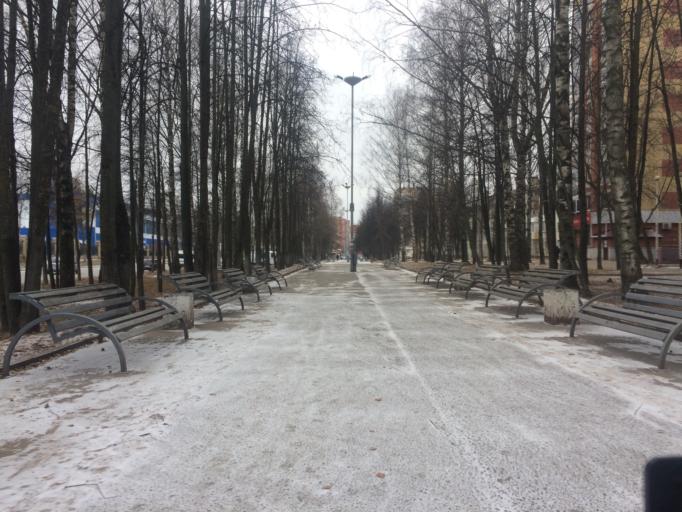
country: RU
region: Mariy-El
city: Yoshkar-Ola
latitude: 56.6430
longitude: 47.8727
